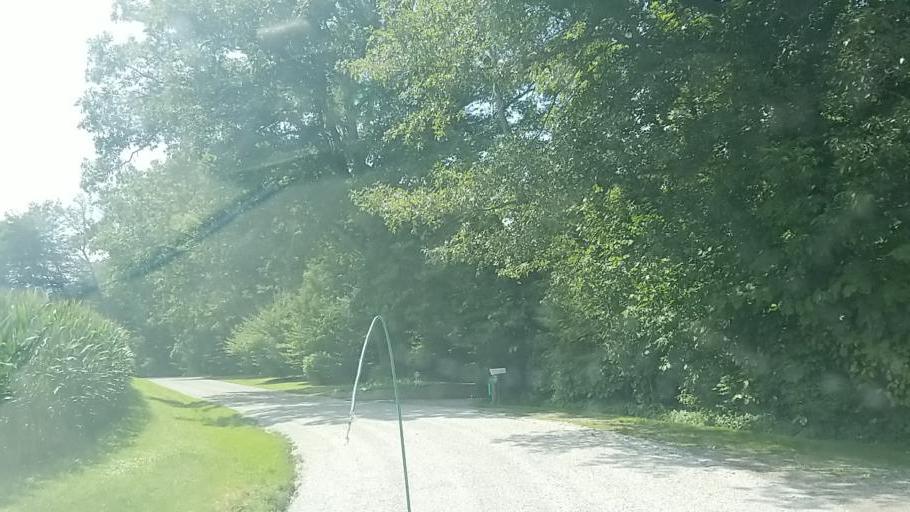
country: US
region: Ohio
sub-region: Sandusky County
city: Bellville
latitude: 40.5914
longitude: -82.5002
